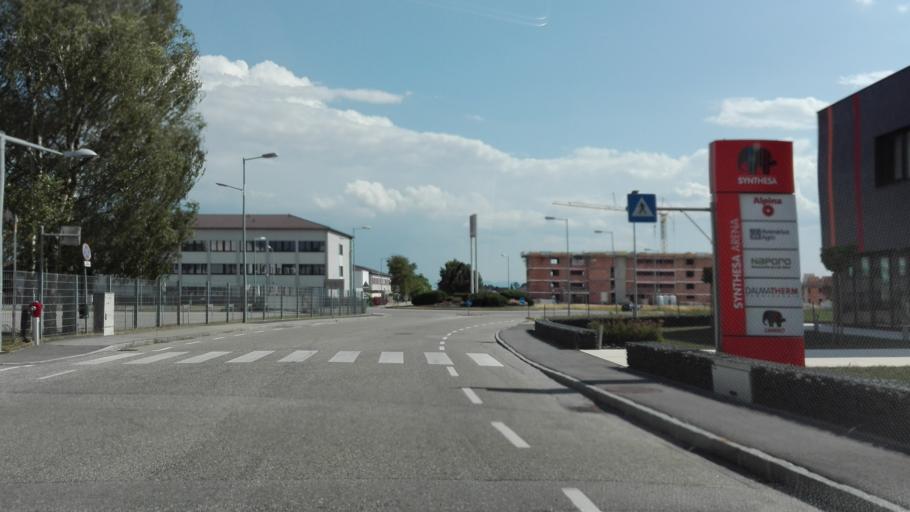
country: AT
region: Upper Austria
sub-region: Politischer Bezirk Perg
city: Perg
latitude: 48.2423
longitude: 14.6359
